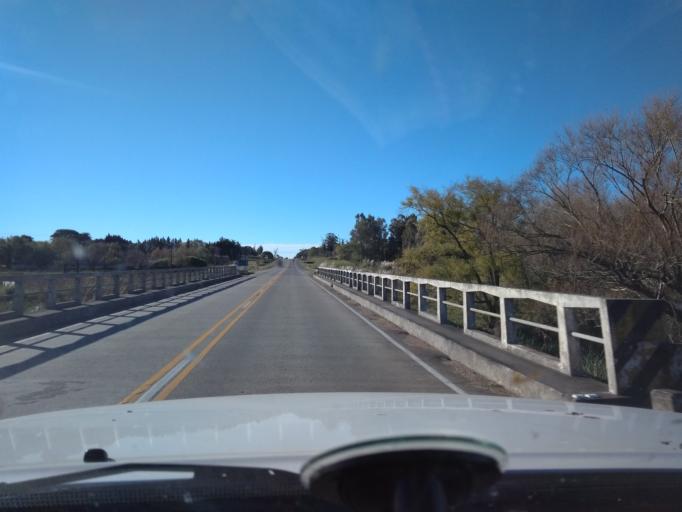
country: UY
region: Canelones
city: Sauce
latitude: -34.6158
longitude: -56.0493
